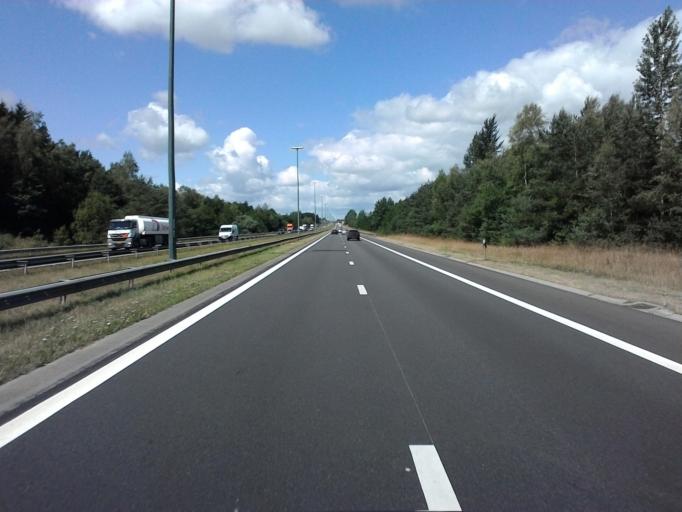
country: BE
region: Wallonia
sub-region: Province du Luxembourg
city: Attert
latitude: 49.6911
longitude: 5.7282
